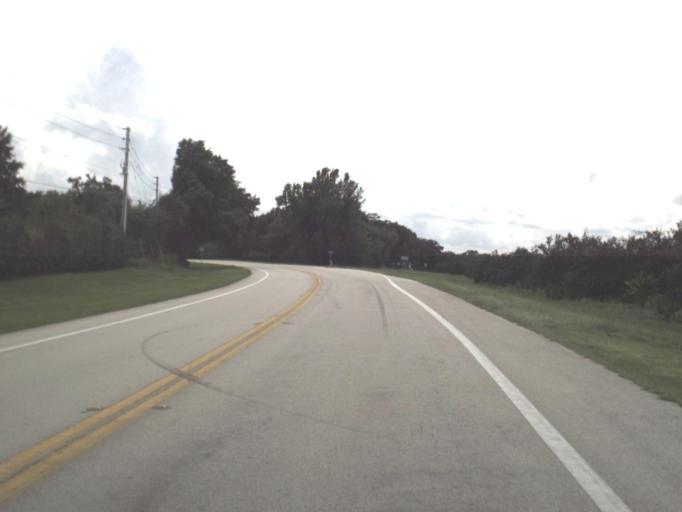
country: US
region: Florida
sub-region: DeSoto County
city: Southeast Arcadia
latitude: 27.1743
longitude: -81.8278
